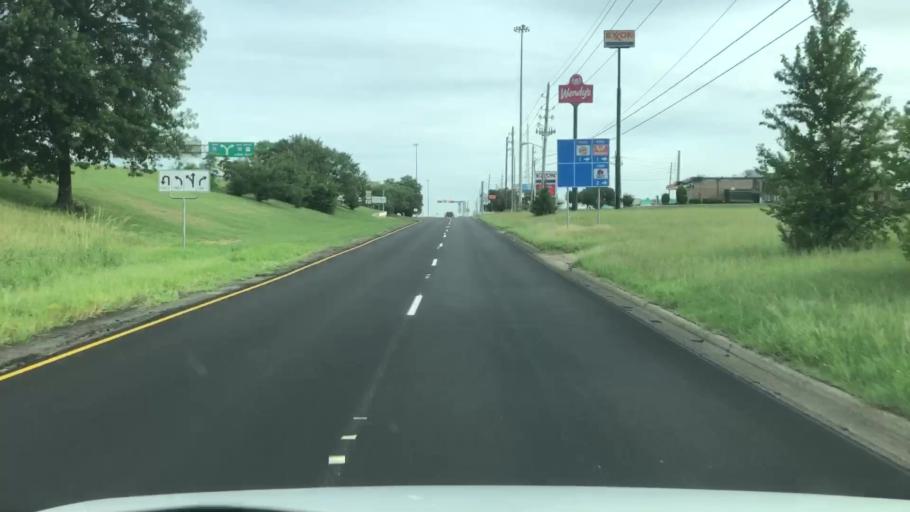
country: US
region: Texas
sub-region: Bowie County
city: Wake Village
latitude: 33.4414
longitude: -94.0962
